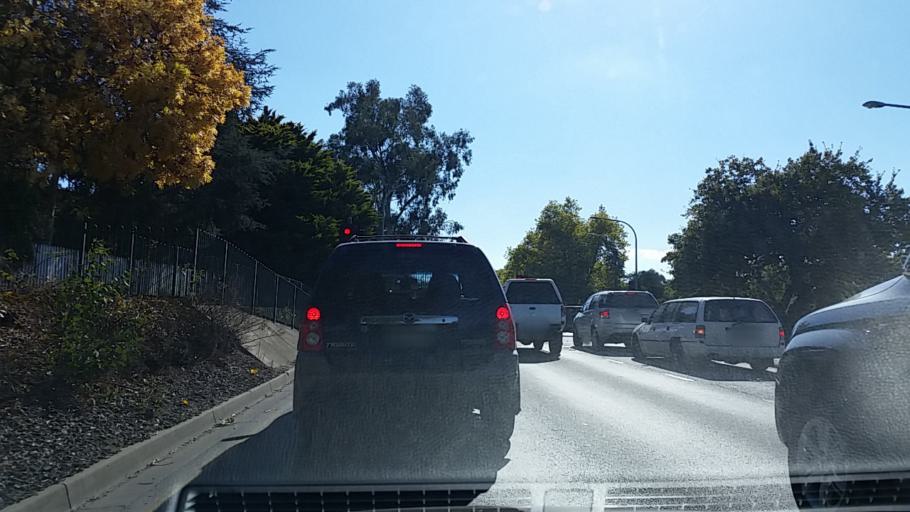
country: AU
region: South Australia
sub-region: Mount Barker
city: Mount Barker
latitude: -35.0657
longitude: 138.8555
